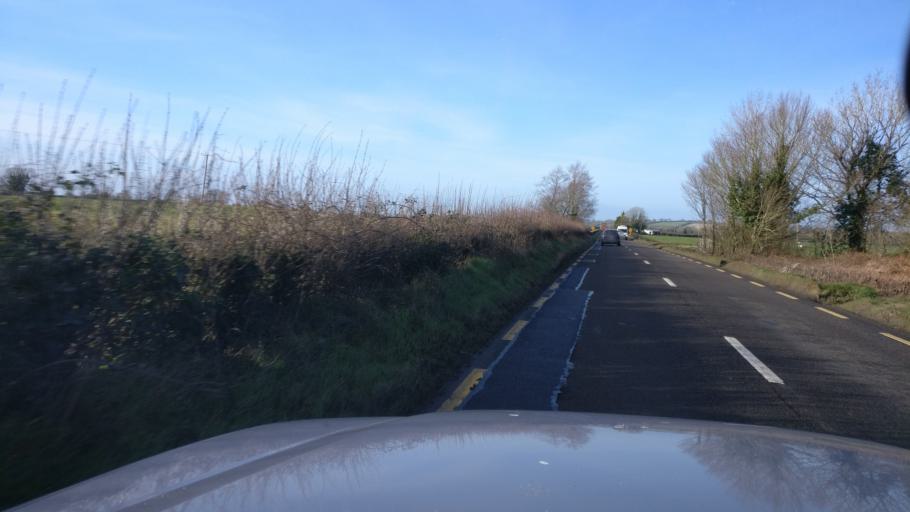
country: IE
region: Leinster
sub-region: Laois
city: Mountmellick
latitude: 53.1744
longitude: -7.3857
